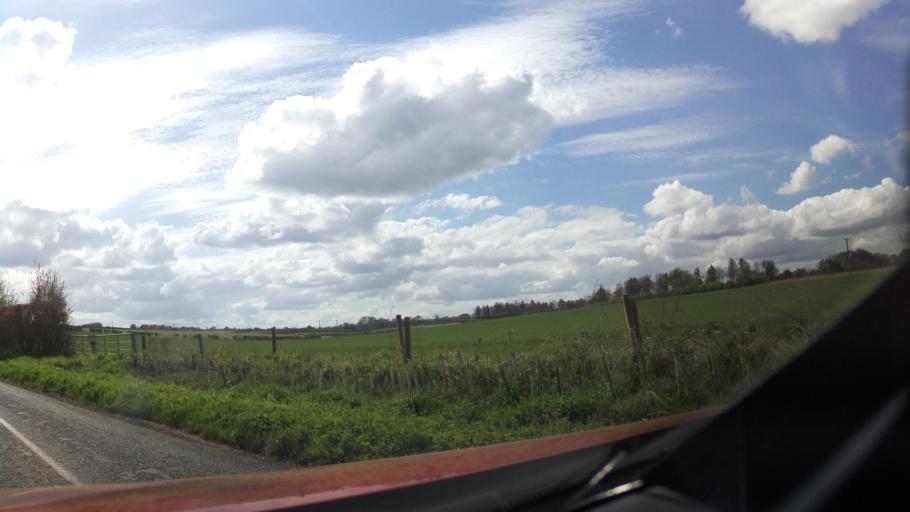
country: GB
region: England
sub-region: Hampshire
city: Andover
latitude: 51.1713
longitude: -1.4841
